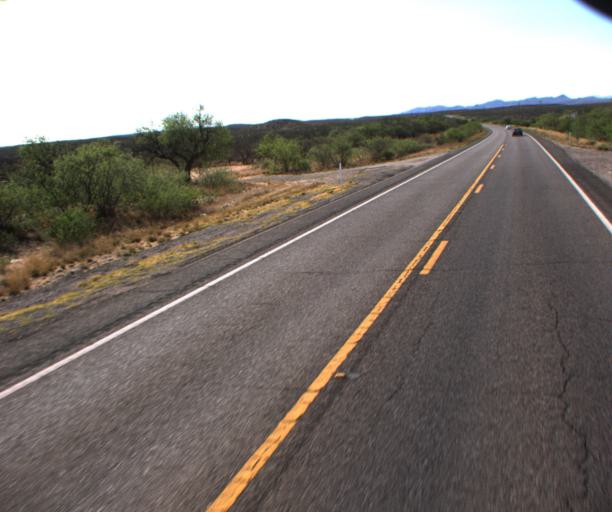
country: US
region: Arizona
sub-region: Cochise County
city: Tombstone
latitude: 31.7938
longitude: -110.1531
